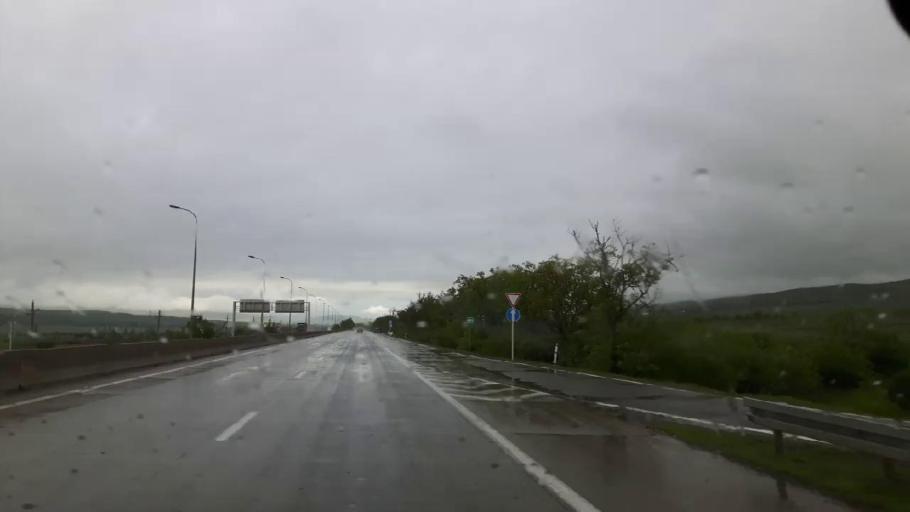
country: GE
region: Shida Kartli
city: Kaspi
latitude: 42.0207
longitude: 44.3006
